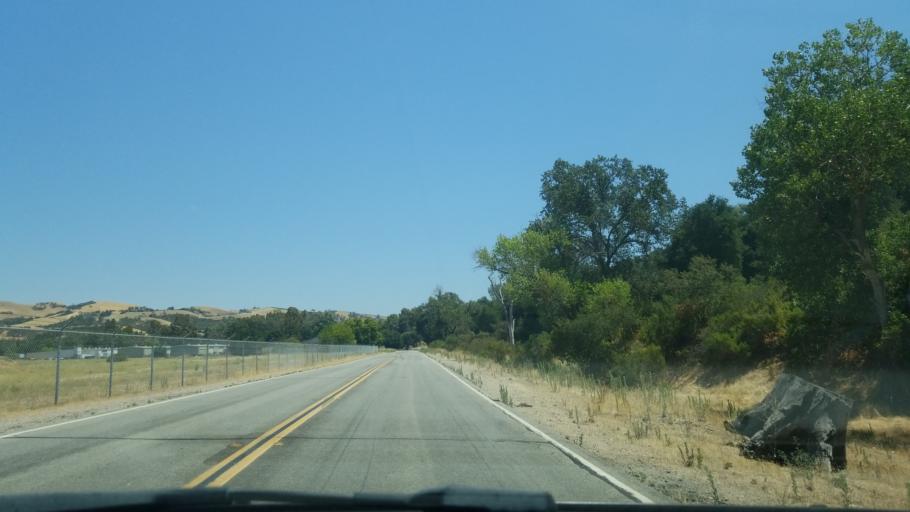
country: US
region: California
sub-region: San Luis Obispo County
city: Atascadero
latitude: 35.4985
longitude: -120.6561
